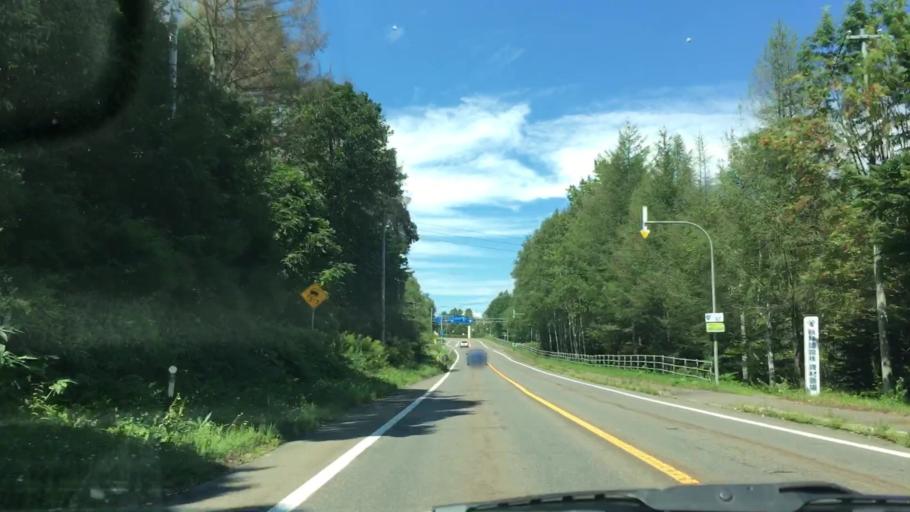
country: JP
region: Hokkaido
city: Otofuke
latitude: 43.2348
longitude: 143.5393
